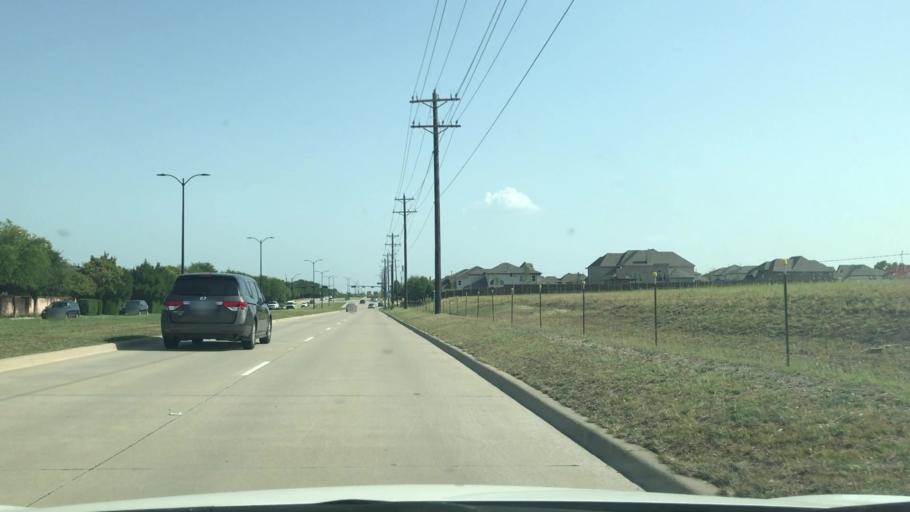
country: US
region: Texas
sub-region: Collin County
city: Frisco
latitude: 33.1334
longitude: -96.7508
